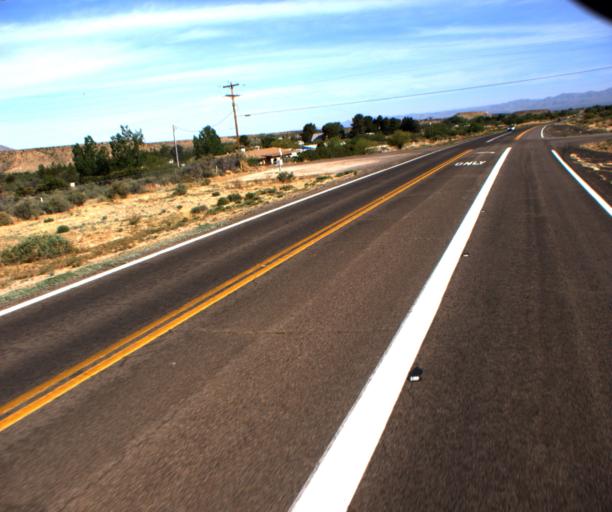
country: US
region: Arizona
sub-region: Graham County
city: Swift Trail Junction
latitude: 32.6859
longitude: -109.7073
